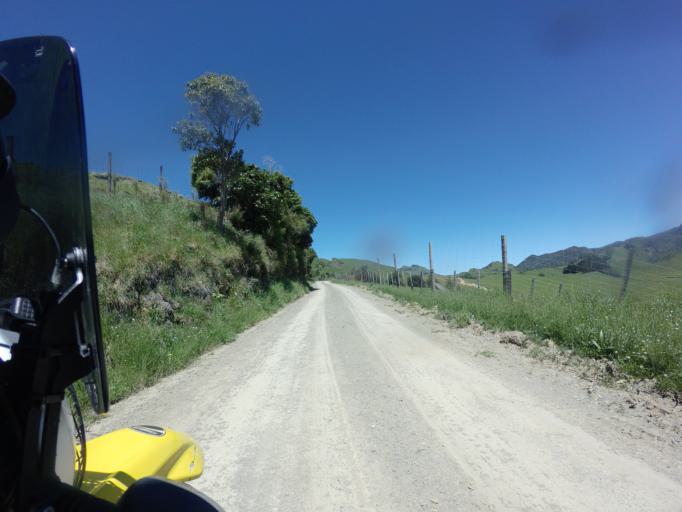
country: NZ
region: Bay of Plenty
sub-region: Opotiki District
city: Opotiki
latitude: -38.4015
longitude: 177.4565
